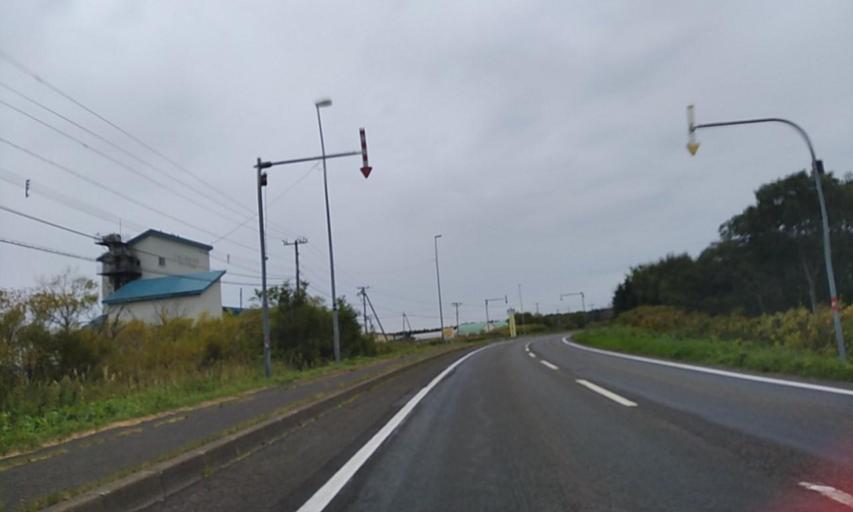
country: JP
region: Hokkaido
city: Makubetsu
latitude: 45.1492
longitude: 142.3485
